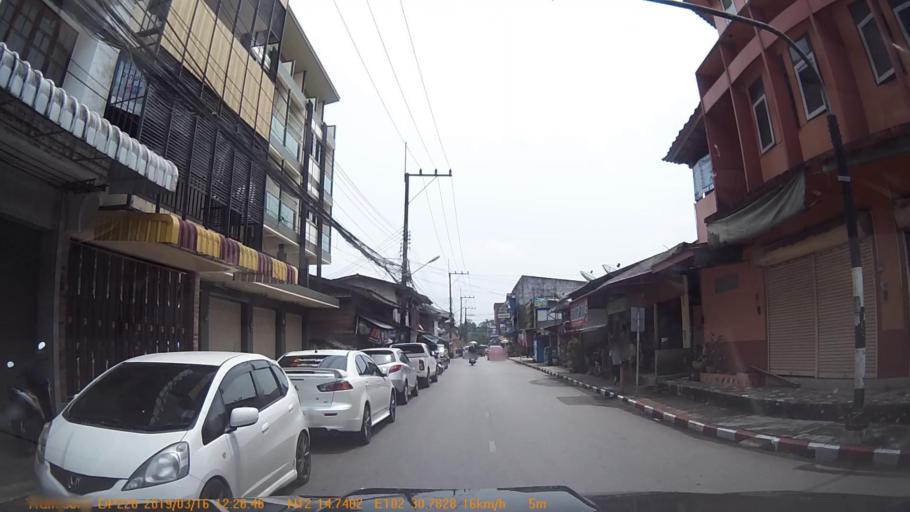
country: TH
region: Trat
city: Trat
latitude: 12.2456
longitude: 102.5131
